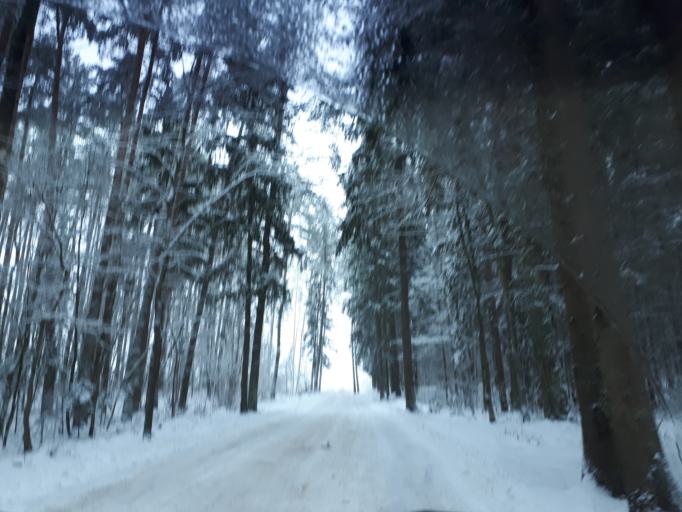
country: BY
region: Vitebsk
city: Vitebsk
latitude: 55.2632
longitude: 30.2130
